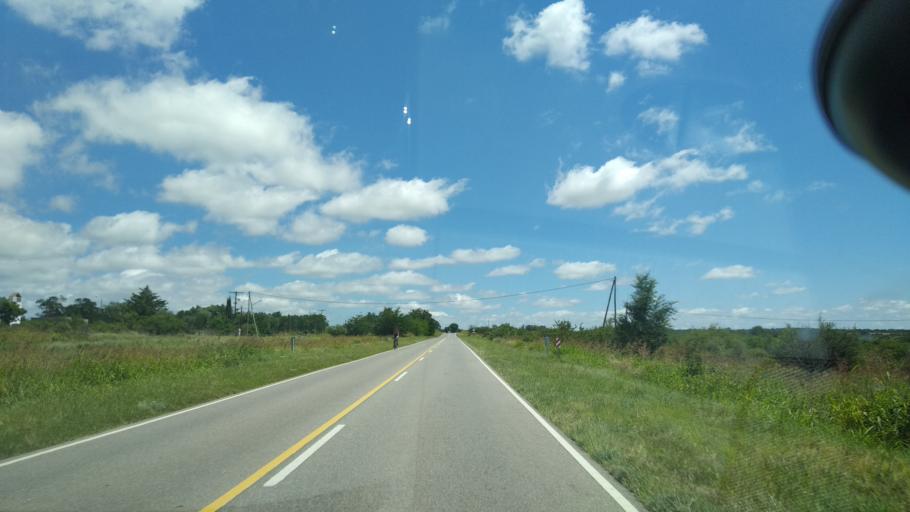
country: AR
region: Cordoba
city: Villa Cura Brochero
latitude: -31.6270
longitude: -65.1072
